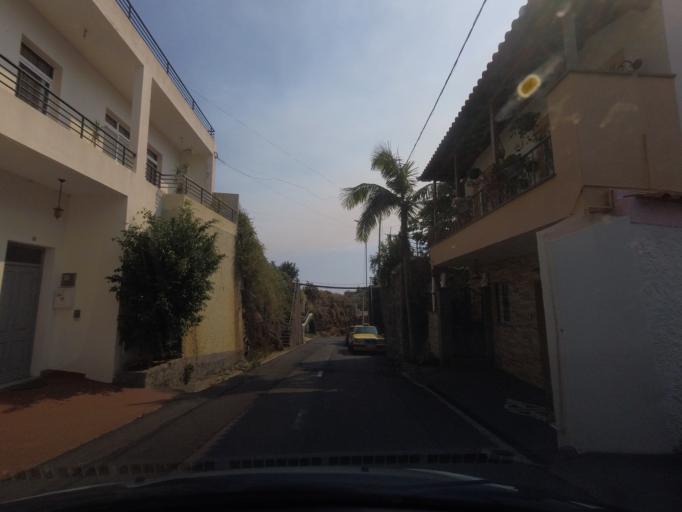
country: PT
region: Madeira
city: Ribeira Brava
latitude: 32.6762
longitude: -17.0664
